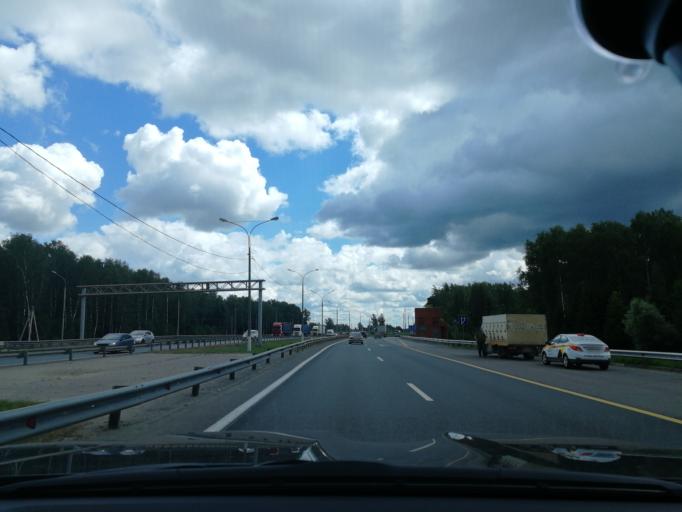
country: RU
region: Moskovskaya
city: Mikhnevo
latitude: 55.1343
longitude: 37.9341
